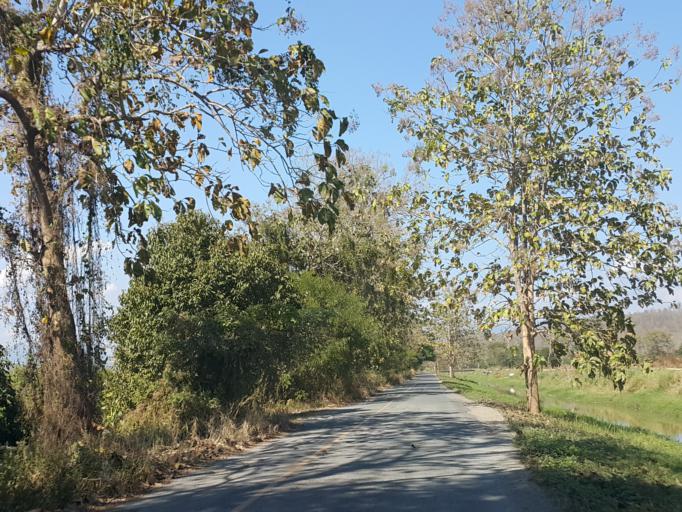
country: TH
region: Chiang Mai
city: Mae Taeng
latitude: 19.0683
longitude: 98.9600
